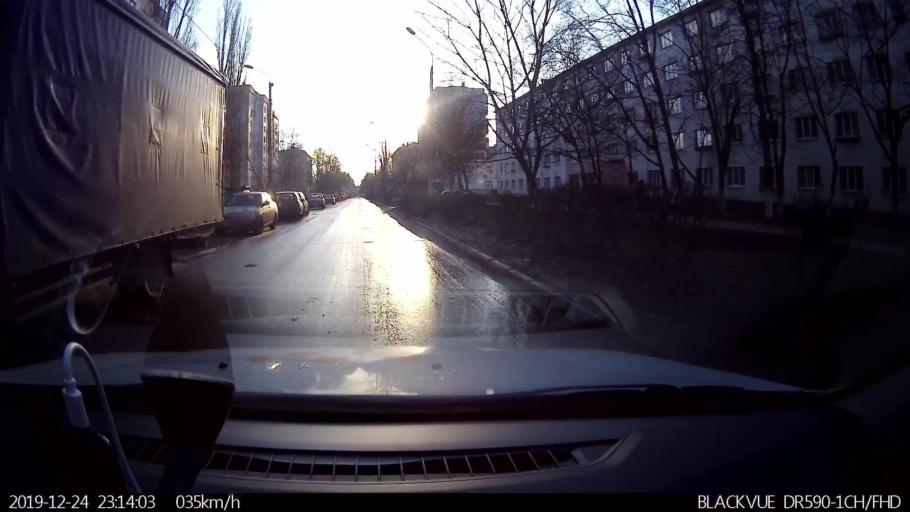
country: RU
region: Nizjnij Novgorod
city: Gorbatovka
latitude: 56.2513
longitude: 43.8585
